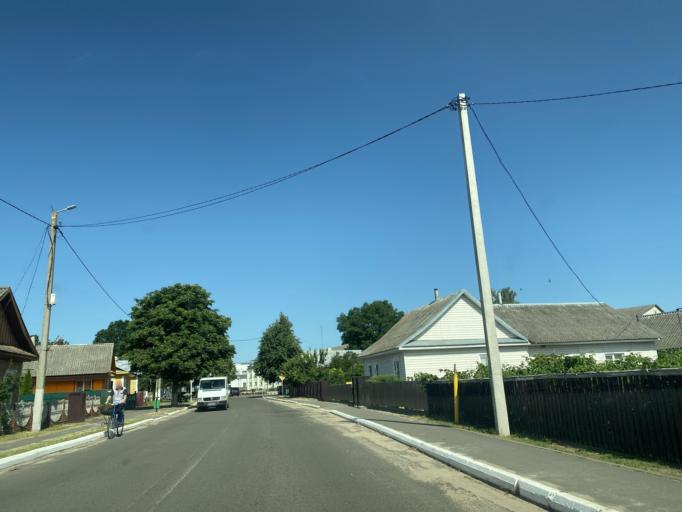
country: BY
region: Brest
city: Ivanava
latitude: 52.3159
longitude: 25.6114
